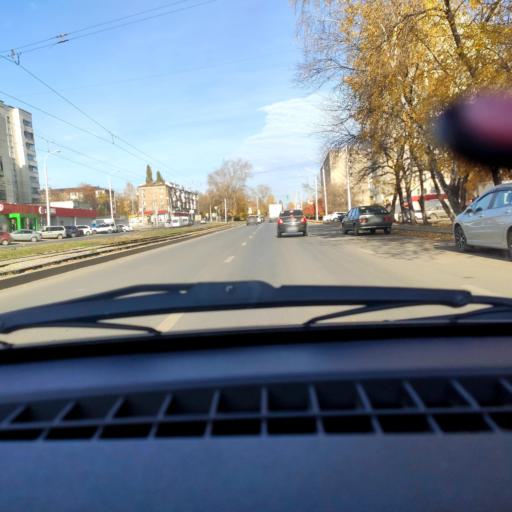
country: RU
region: Bashkortostan
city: Ufa
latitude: 54.8117
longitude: 56.1288
